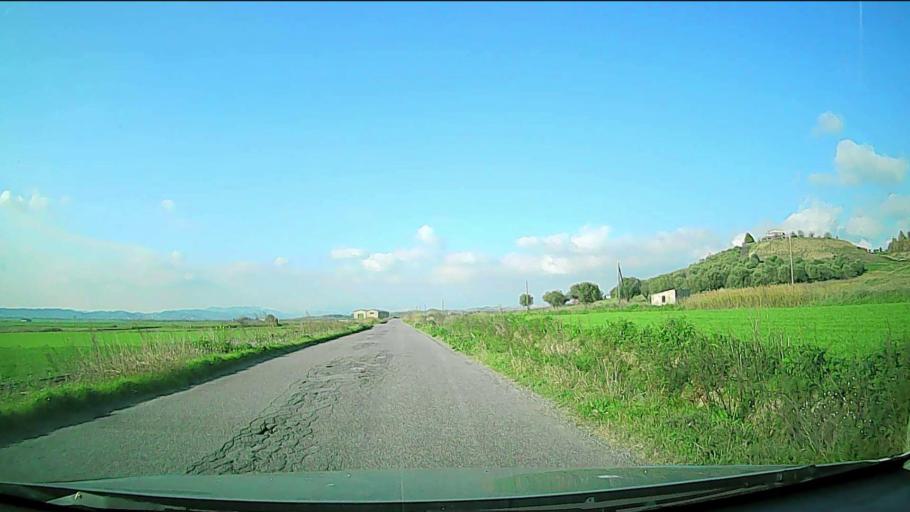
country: IT
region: Calabria
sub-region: Provincia di Crotone
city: Tronca
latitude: 39.2007
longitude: 17.0895
